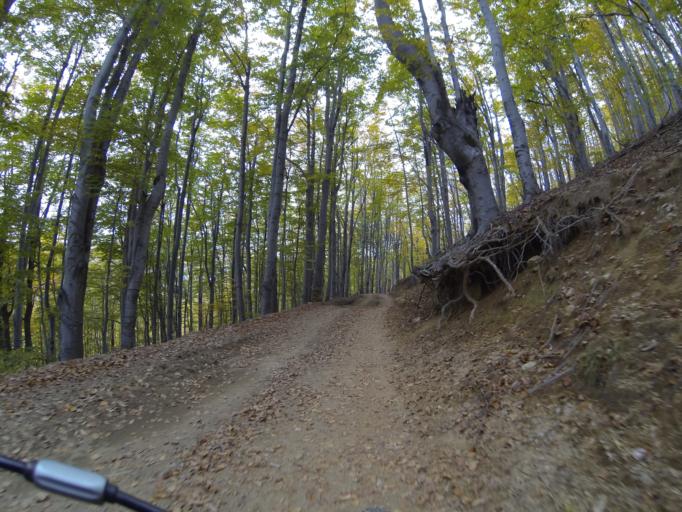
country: RO
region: Gorj
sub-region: Comuna Pades
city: Closani
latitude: 45.0875
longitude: 22.8391
